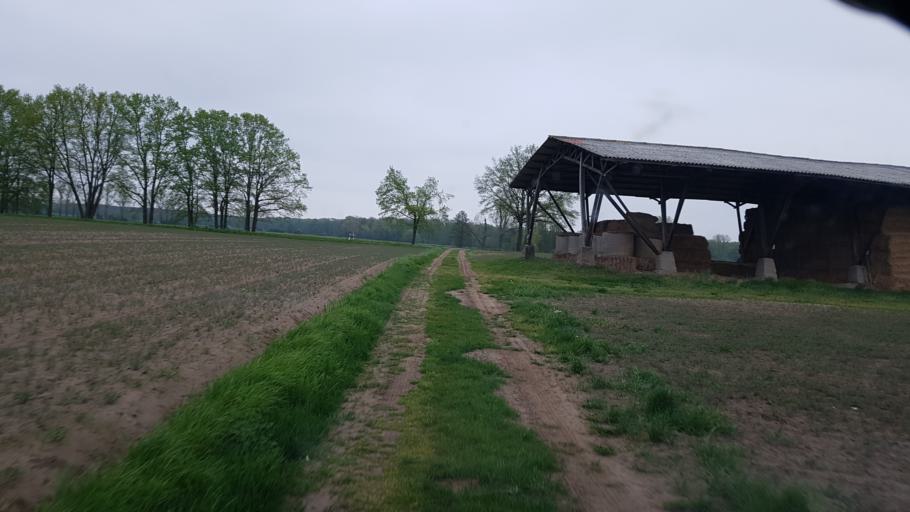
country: DE
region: Brandenburg
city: Schonewalde
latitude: 51.6995
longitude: 13.6080
